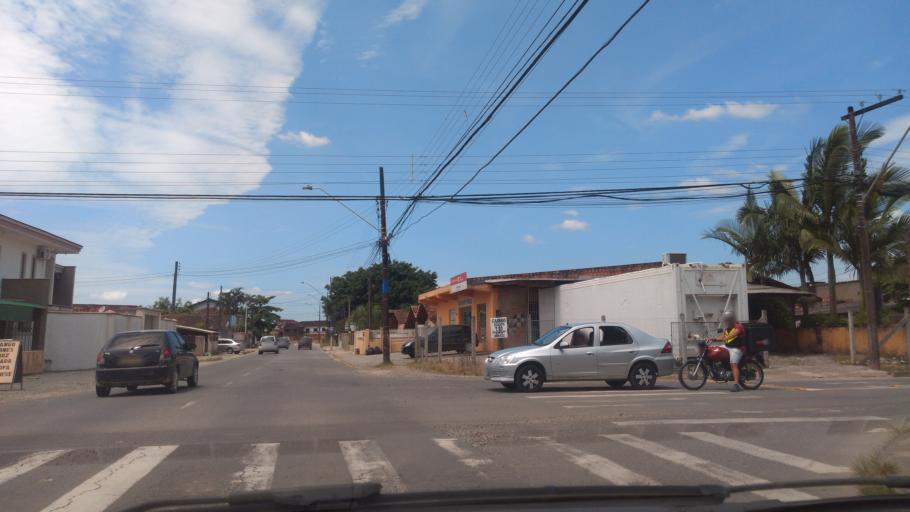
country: BR
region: Santa Catarina
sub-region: Joinville
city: Joinville
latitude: -26.3227
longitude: -48.8152
